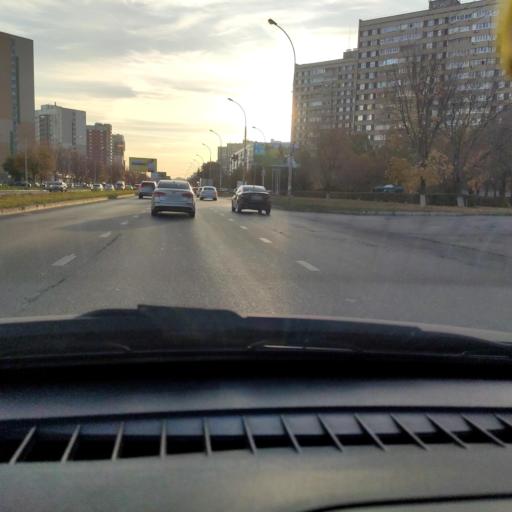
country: RU
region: Samara
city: Tol'yatti
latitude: 53.5312
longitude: 49.3410
